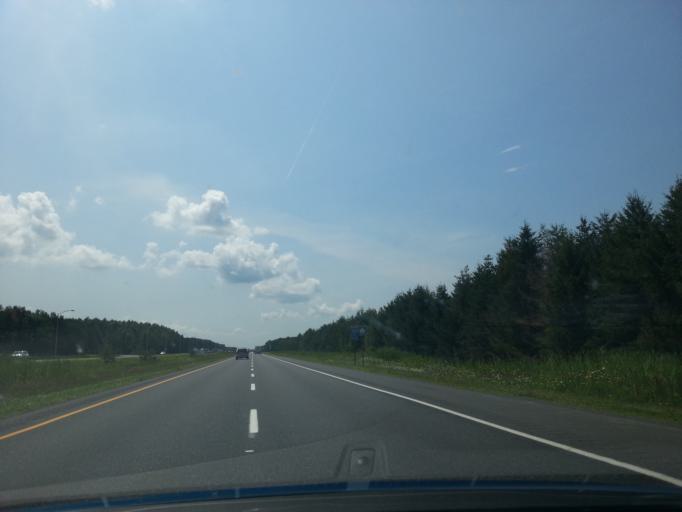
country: CA
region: Quebec
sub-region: Mauricie
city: Daveluyville
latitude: 46.1691
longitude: -72.1355
